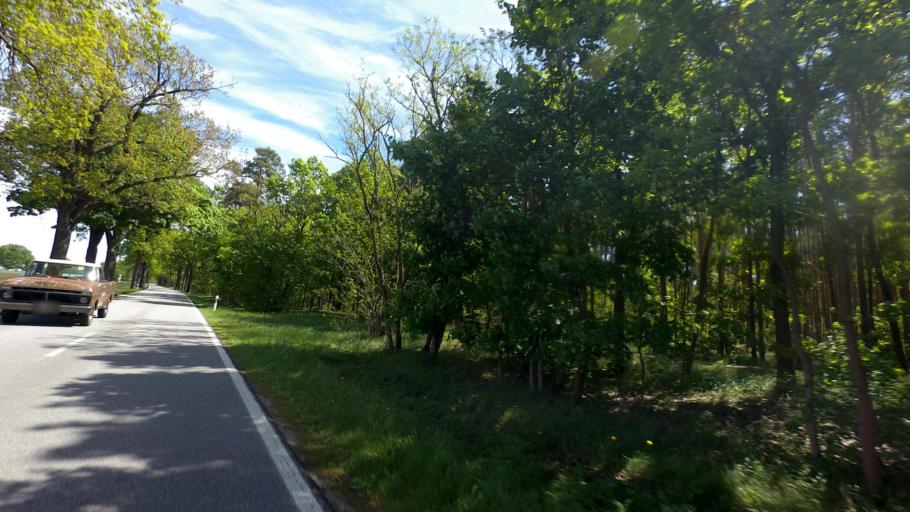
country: DE
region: Brandenburg
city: Sperenberg
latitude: 52.0470
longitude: 13.3976
